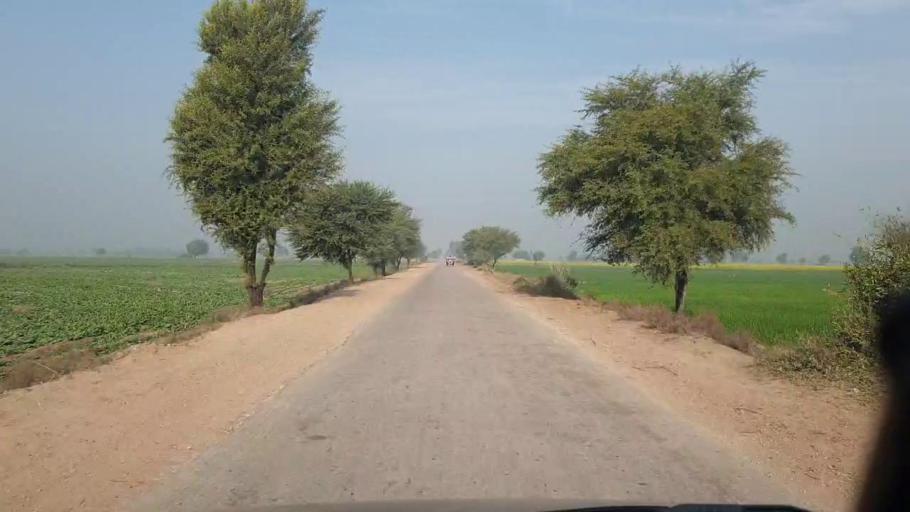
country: PK
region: Sindh
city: Shahdadpur
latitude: 25.9728
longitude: 68.5774
